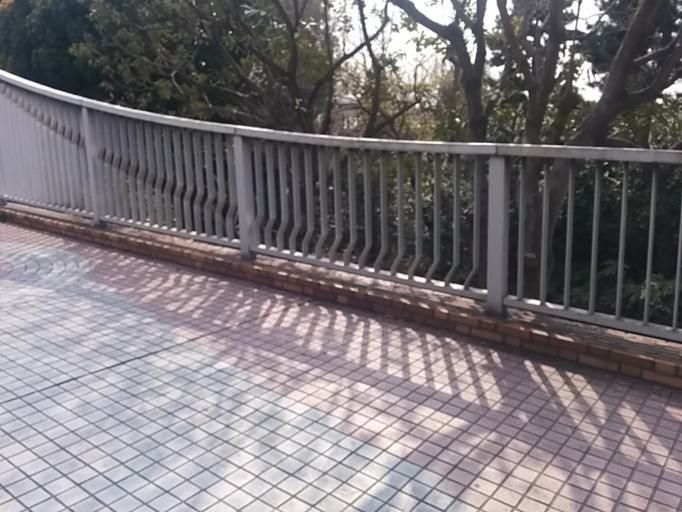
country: JP
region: Tokyo
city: Urayasu
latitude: 35.6474
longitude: 139.8561
